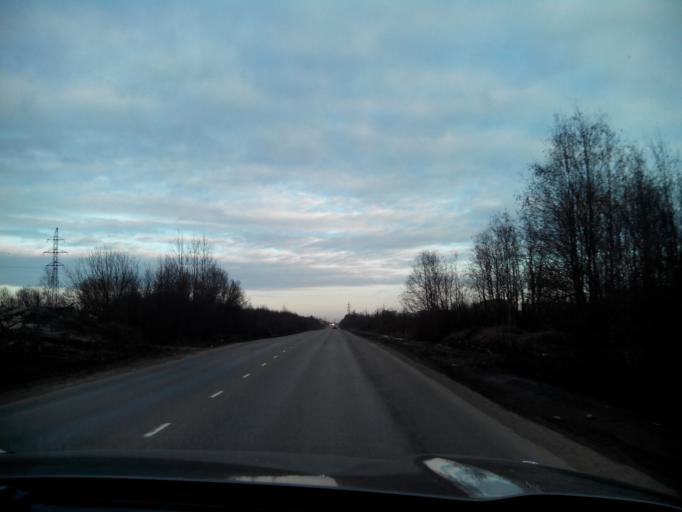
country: RU
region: Arkhangelskaya
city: Arkhangel'sk
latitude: 64.5254
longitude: 40.6635
